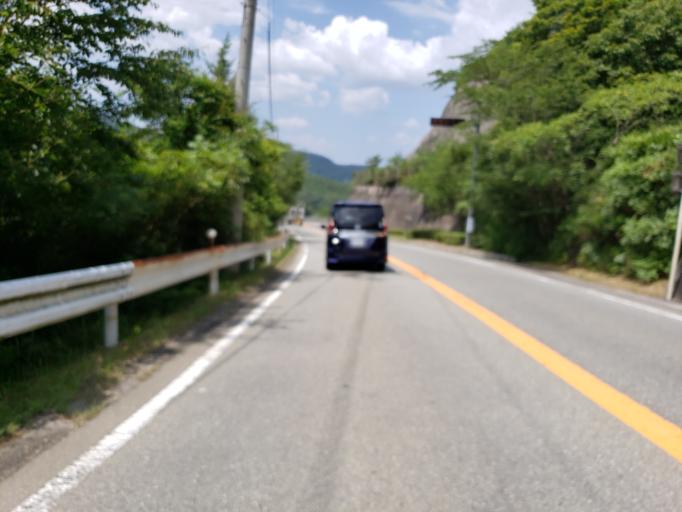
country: JP
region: Hyogo
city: Aioi
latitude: 34.7968
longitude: 134.4489
